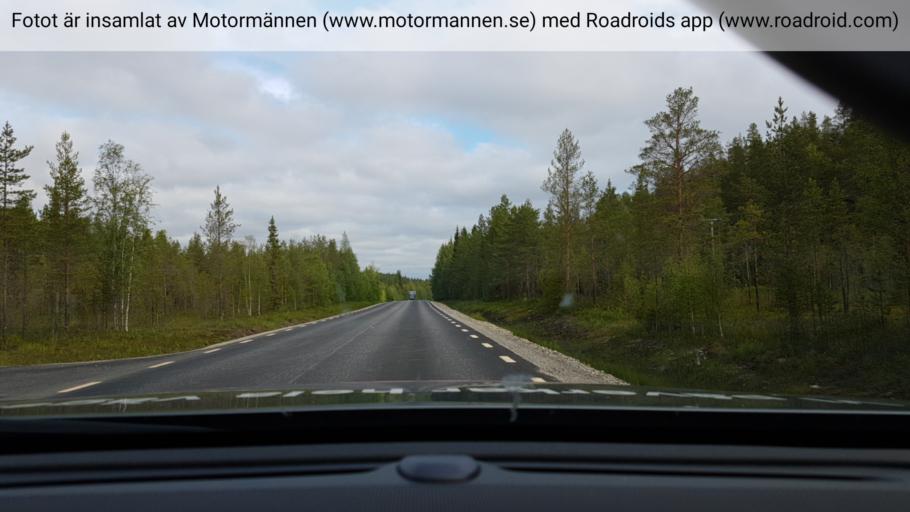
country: SE
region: Vaesterbotten
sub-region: Vindelns Kommun
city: Vindeln
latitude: 64.4544
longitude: 19.3354
